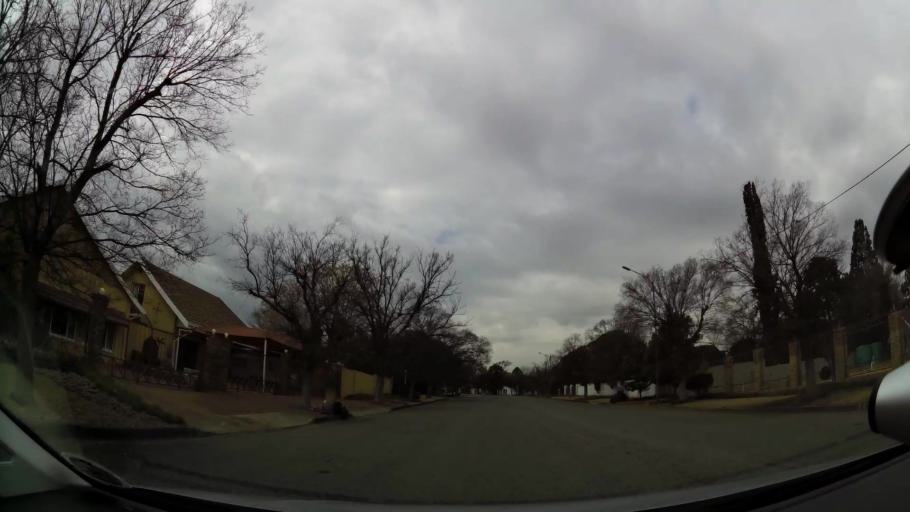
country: ZA
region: Orange Free State
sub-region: Fezile Dabi District Municipality
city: Kroonstad
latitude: -27.6759
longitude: 27.2427
